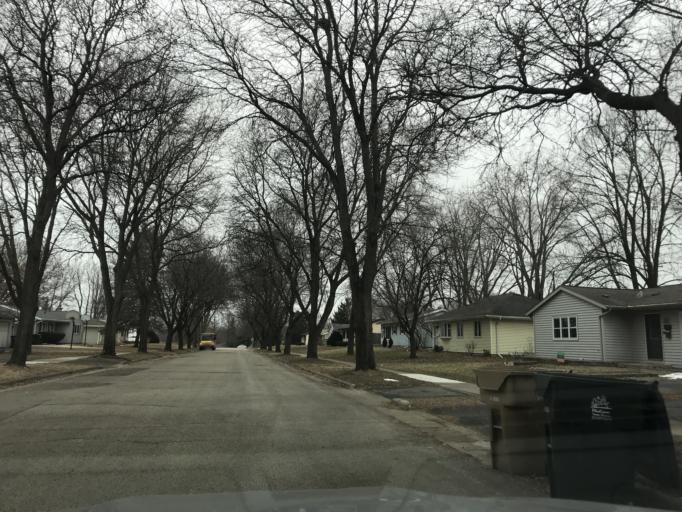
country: US
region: Wisconsin
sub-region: Dane County
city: Monona
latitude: 43.0954
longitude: -89.3107
